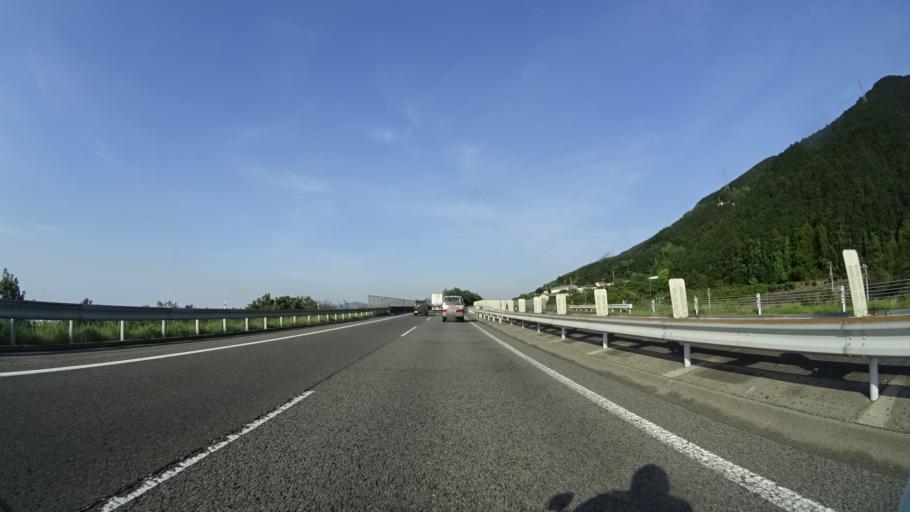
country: JP
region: Ehime
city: Kawanoecho
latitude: 33.9635
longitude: 133.5256
